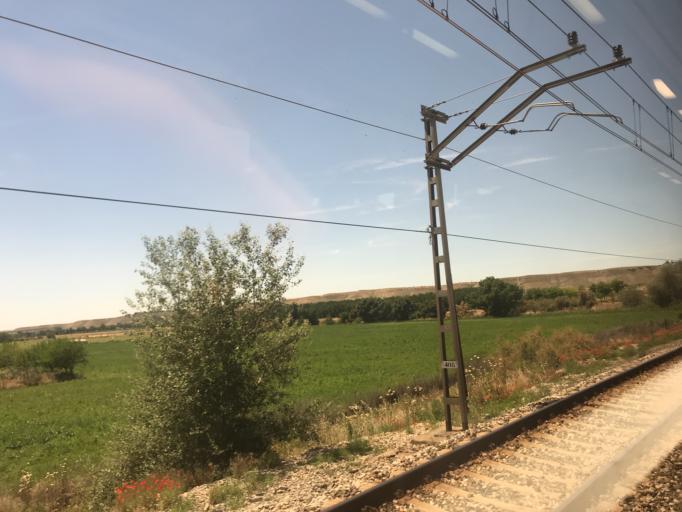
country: ES
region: Madrid
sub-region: Provincia de Madrid
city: Aranjuez
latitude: 40.0515
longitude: -3.6303
